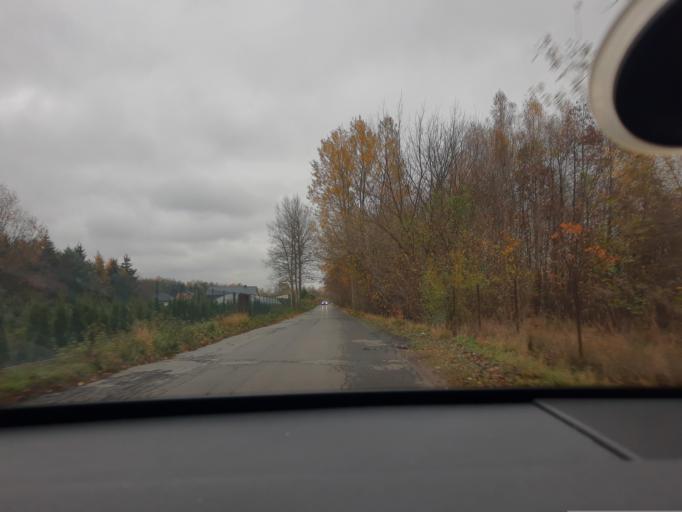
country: PL
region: Lodz Voivodeship
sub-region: Powiat pabianicki
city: Konstantynow Lodzki
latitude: 51.7510
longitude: 19.3726
